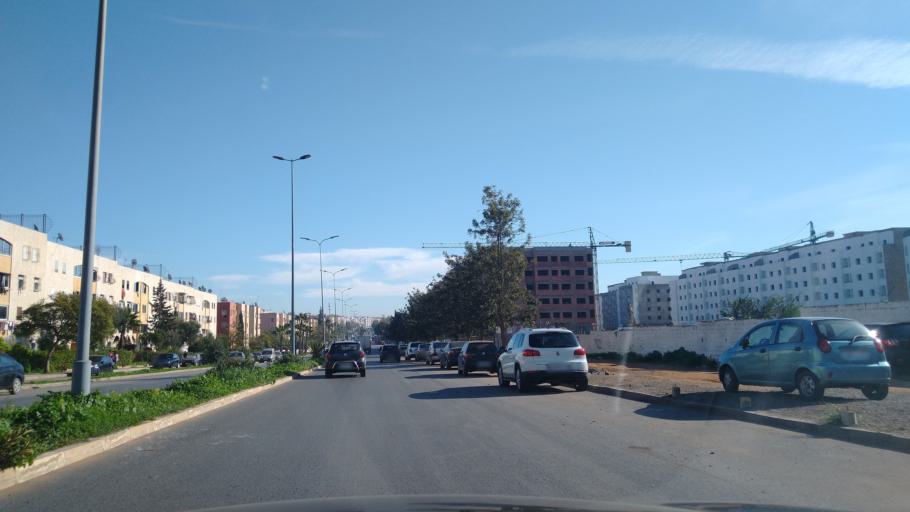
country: MA
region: Rabat-Sale-Zemmour-Zaer
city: Sale
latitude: 33.9969
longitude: -6.7476
